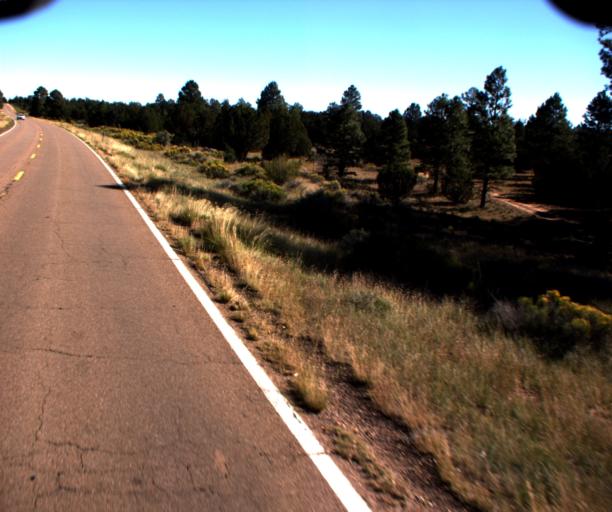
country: US
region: Arizona
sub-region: Navajo County
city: Heber-Overgaard
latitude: 34.4355
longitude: -110.5380
